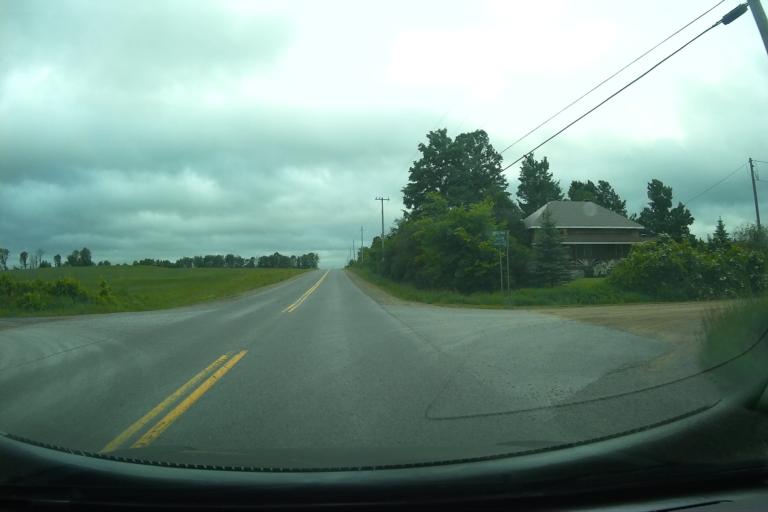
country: CA
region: Ontario
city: Pembroke
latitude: 45.5021
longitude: -77.1355
